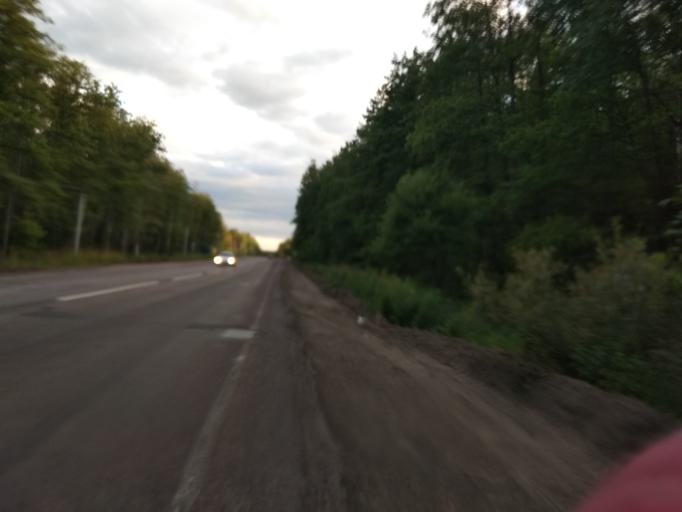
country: RU
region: Moskovskaya
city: Misheronskiy
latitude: 55.6357
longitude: 39.7481
